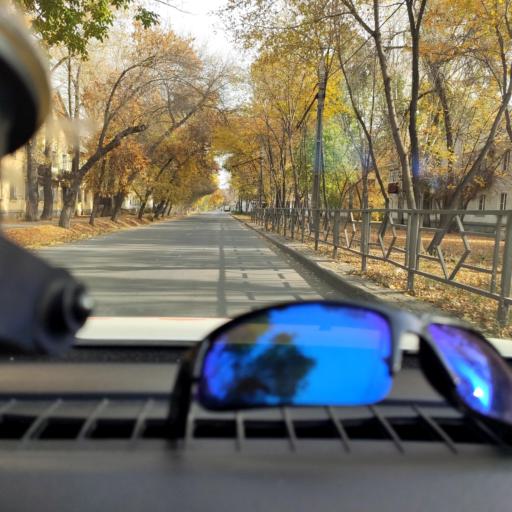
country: RU
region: Samara
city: Samara
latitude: 53.1136
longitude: 50.0733
